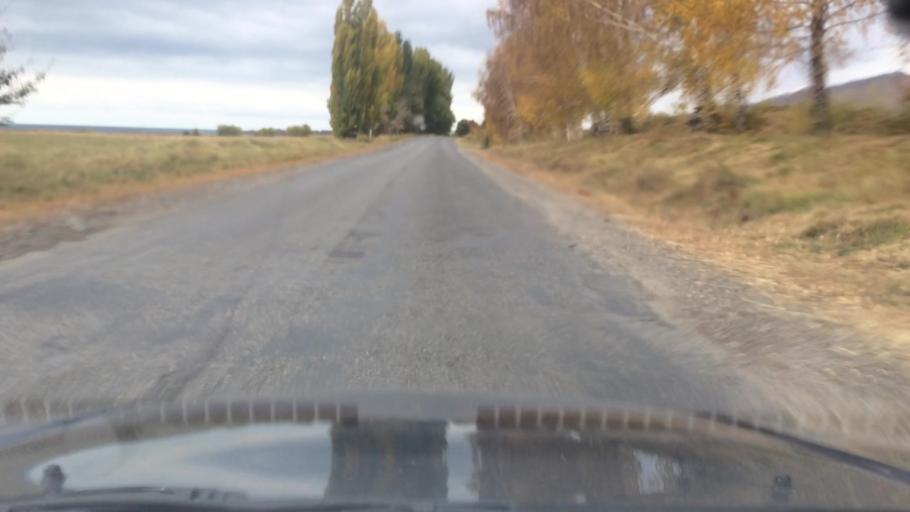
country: KG
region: Ysyk-Koel
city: Tyup
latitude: 42.7637
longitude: 78.1731
